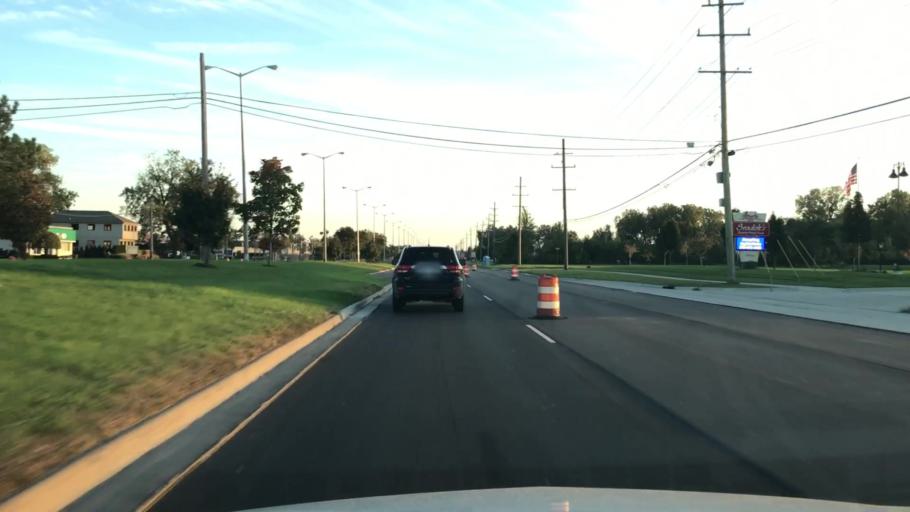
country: US
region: Michigan
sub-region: Macomb County
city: Sterling Heights
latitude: 42.5904
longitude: -83.0505
